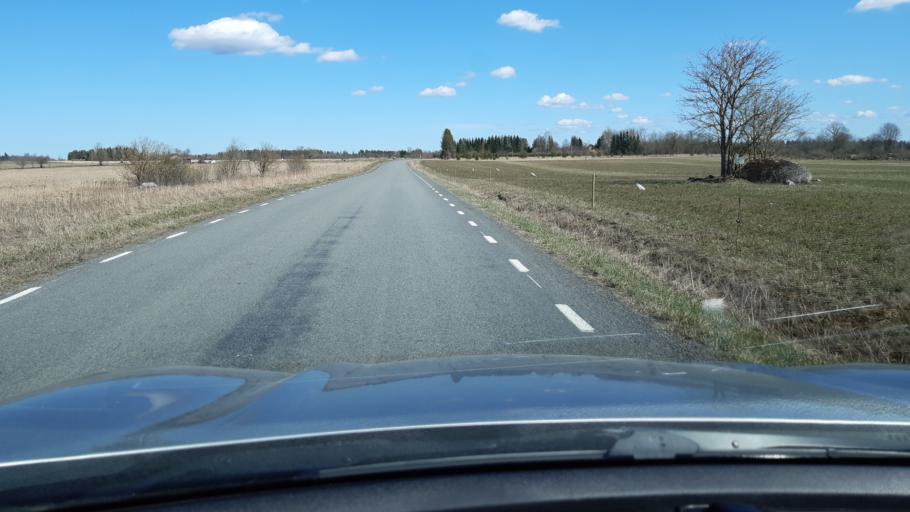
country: EE
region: Raplamaa
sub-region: Kohila vald
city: Kohila
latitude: 59.1830
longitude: 24.8611
